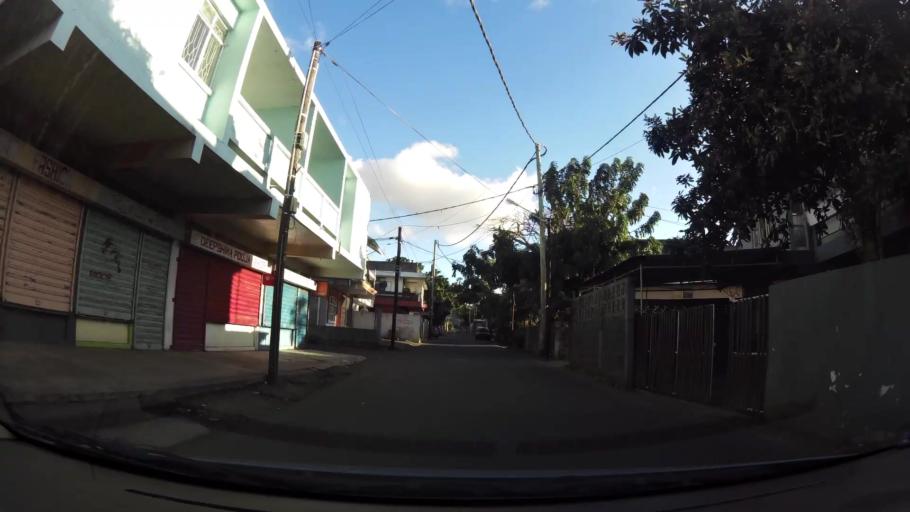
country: MU
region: Plaines Wilhems
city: Quatre Bornes
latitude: -20.2539
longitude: 57.4712
